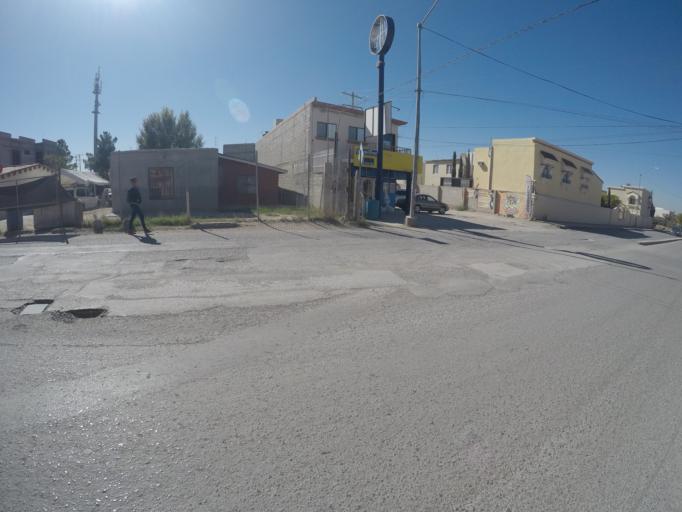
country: US
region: Texas
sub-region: El Paso County
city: Socorro
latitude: 31.6926
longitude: -106.3659
